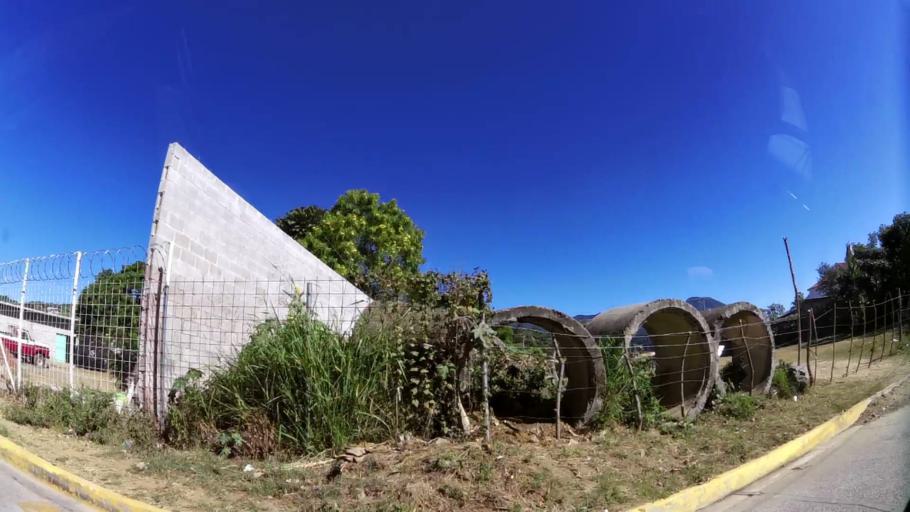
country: SV
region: Sonsonate
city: Juayua
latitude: 13.8423
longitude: -89.7487
